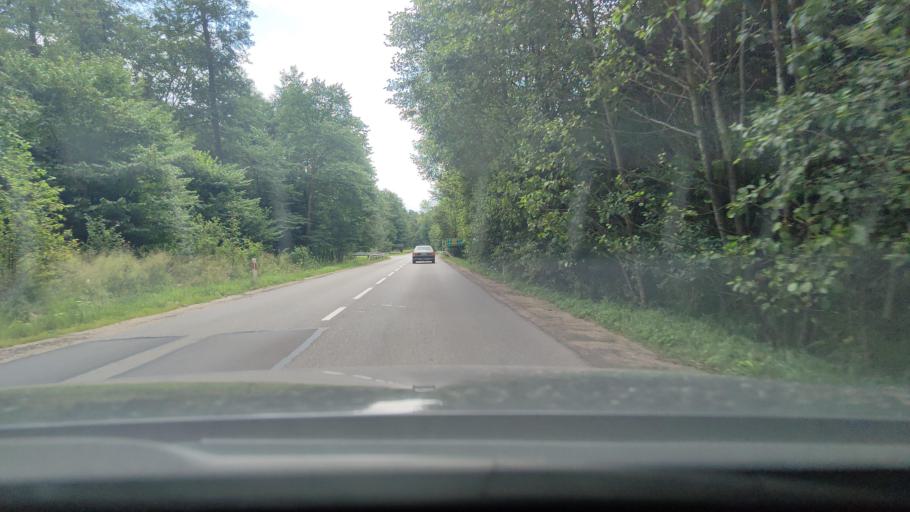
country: PL
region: Pomeranian Voivodeship
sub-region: Powiat wejherowski
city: Wejherowo
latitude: 54.5744
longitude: 18.2515
